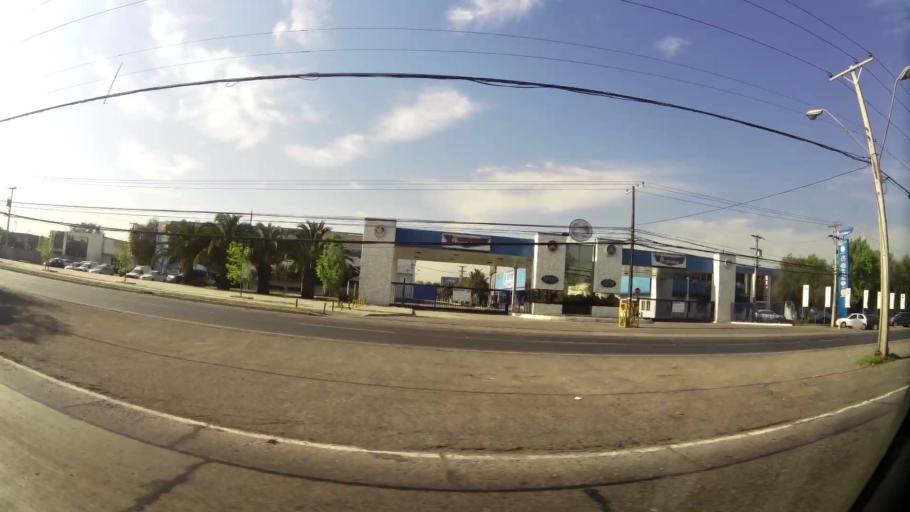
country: CL
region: Santiago Metropolitan
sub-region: Provincia de Santiago
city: Lo Prado
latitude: -33.5128
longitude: -70.7292
